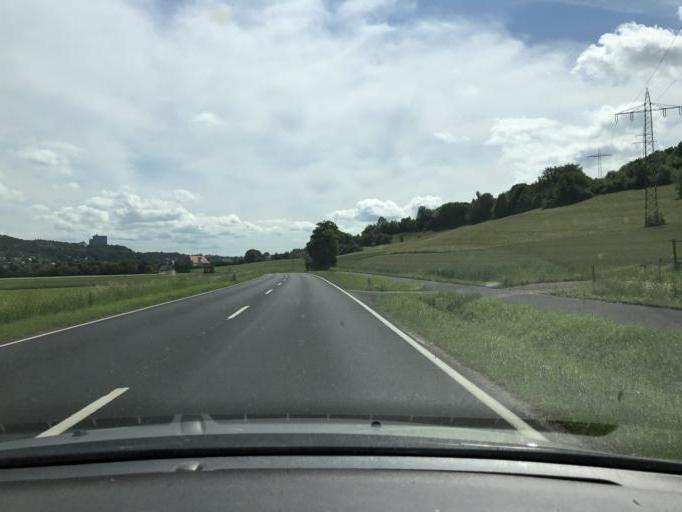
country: DE
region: Hesse
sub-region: Regierungsbezirk Kassel
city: Rotenburg an der Fulda
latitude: 51.0020
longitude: 9.7011
